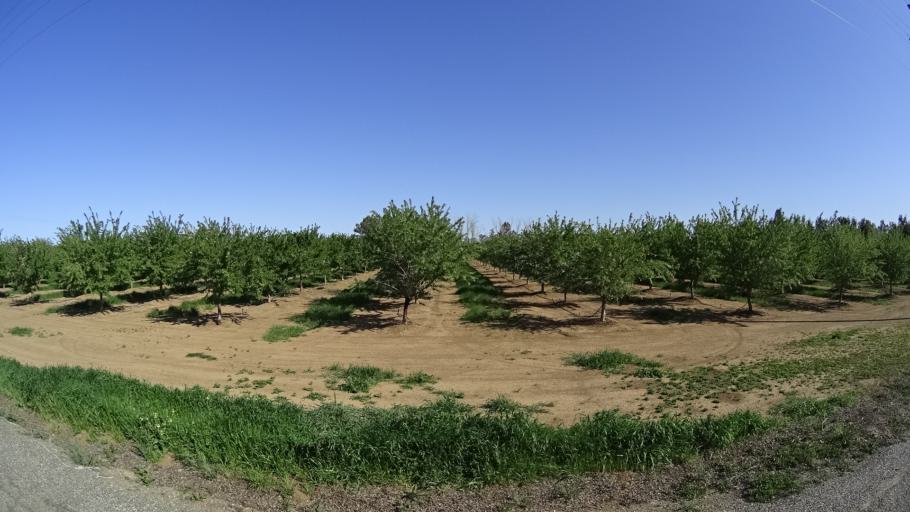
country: US
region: California
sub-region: Glenn County
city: Hamilton City
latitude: 39.7757
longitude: -122.0940
